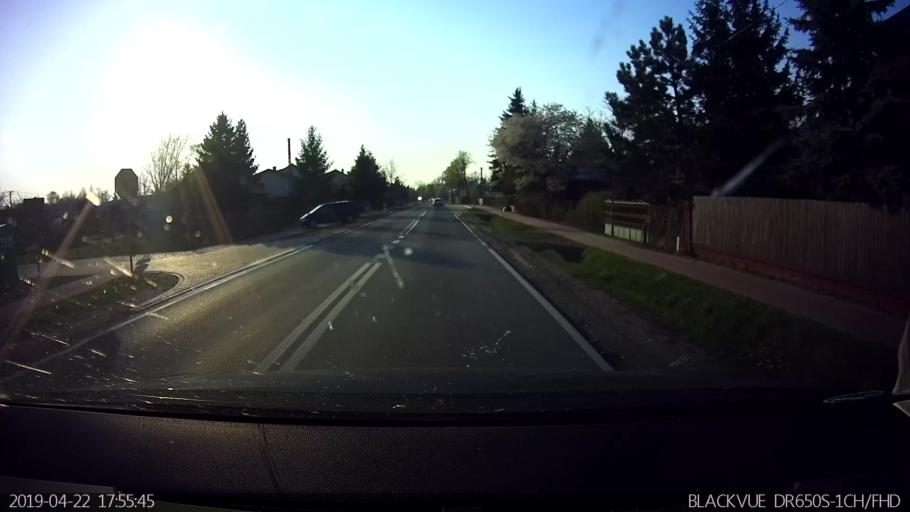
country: PL
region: Masovian Voivodeship
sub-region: Powiat wegrowski
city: Korytnica
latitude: 52.4627
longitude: 21.9155
